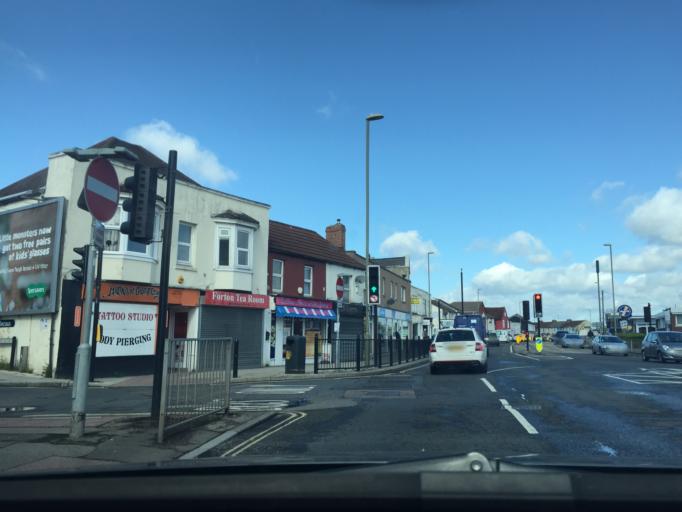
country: GB
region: England
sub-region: Hampshire
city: Gosport
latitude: 50.8003
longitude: -1.1409
